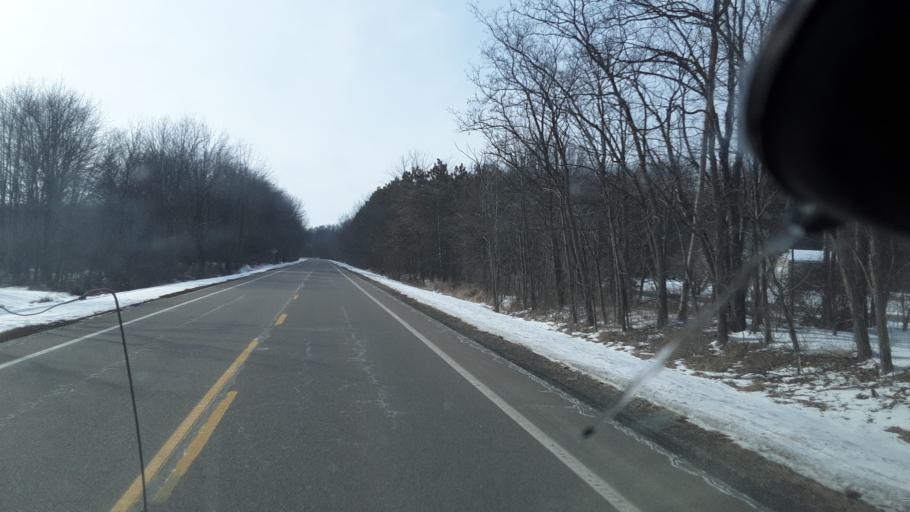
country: US
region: Ohio
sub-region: Portage County
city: Ravenna
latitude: 41.0332
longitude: -81.1960
